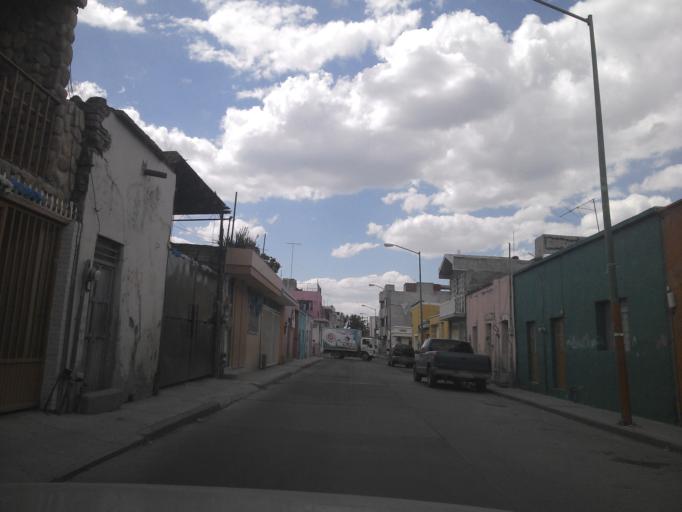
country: MX
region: Guanajuato
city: San Francisco del Rincon
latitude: 21.0229
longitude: -101.8569
